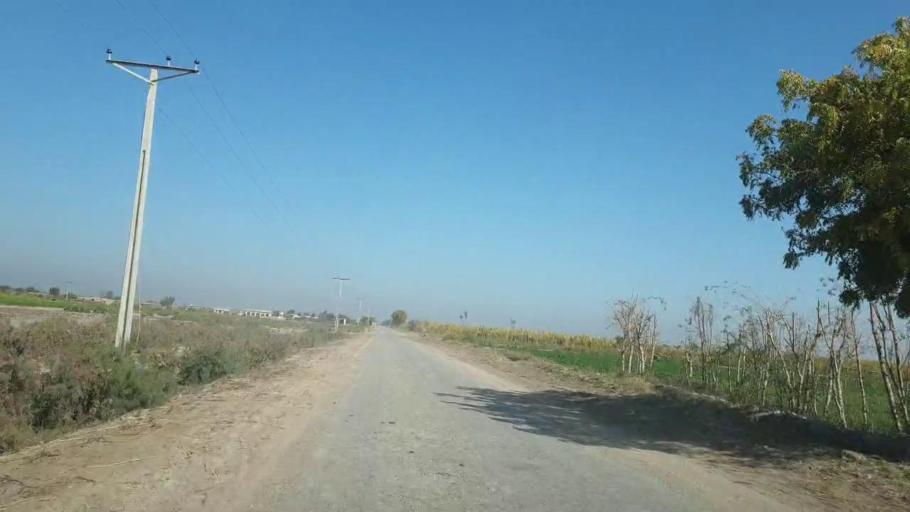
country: PK
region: Sindh
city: Mirpur Khas
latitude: 25.5932
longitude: 69.0453
